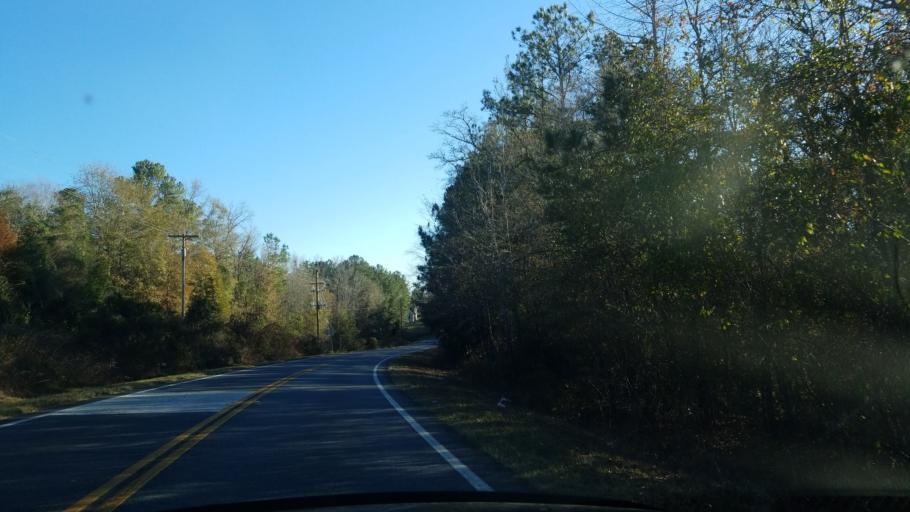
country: US
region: Georgia
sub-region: Talbot County
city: Talbotton
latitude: 32.5622
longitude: -84.6048
